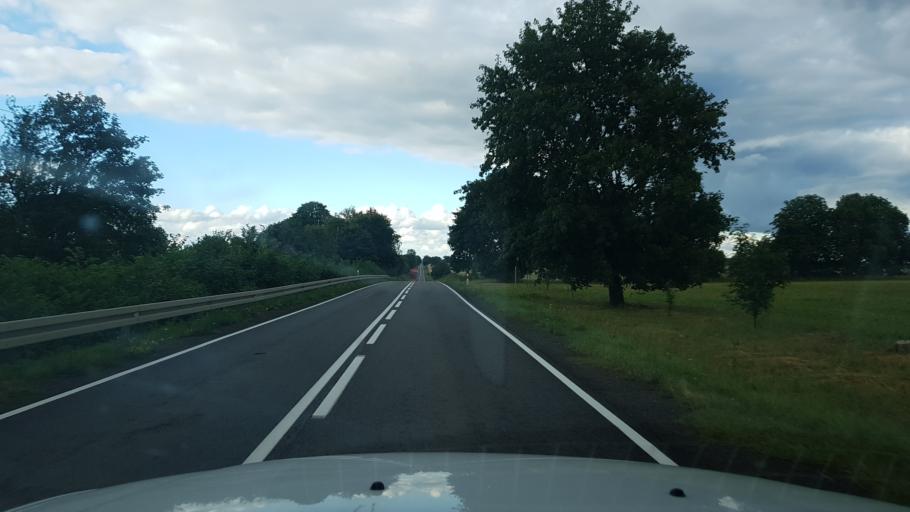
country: PL
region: West Pomeranian Voivodeship
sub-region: Powiat drawski
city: Drawsko Pomorskie
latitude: 53.5023
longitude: 15.7477
